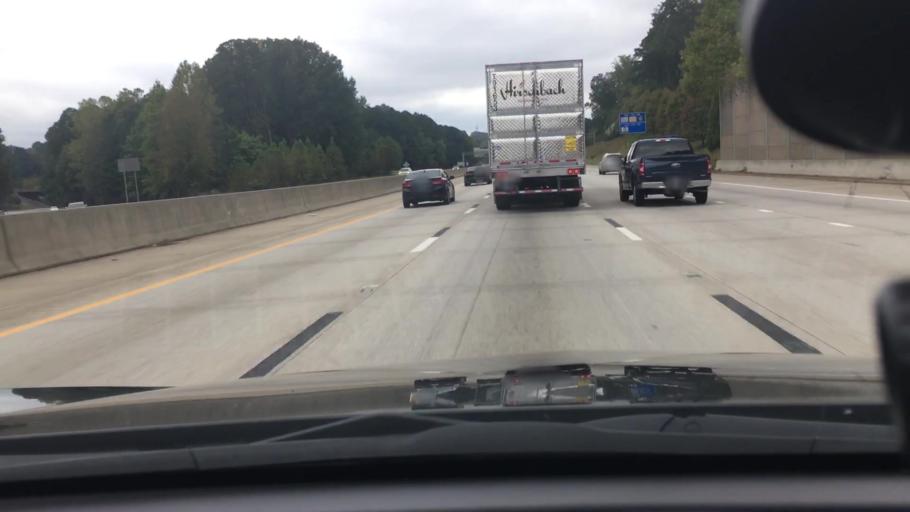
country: US
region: North Carolina
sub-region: Wake County
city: Cary
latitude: 35.7405
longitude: -78.7863
